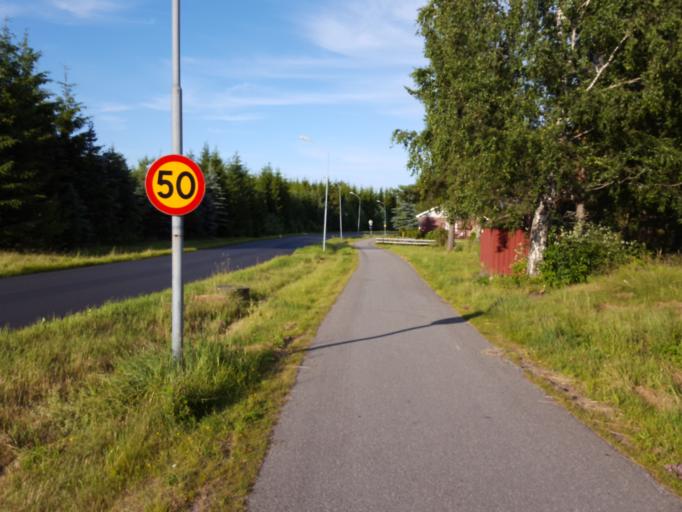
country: SE
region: Uppsala
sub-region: Osthammars Kommun
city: OEsthammar
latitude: 60.2603
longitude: 18.3501
